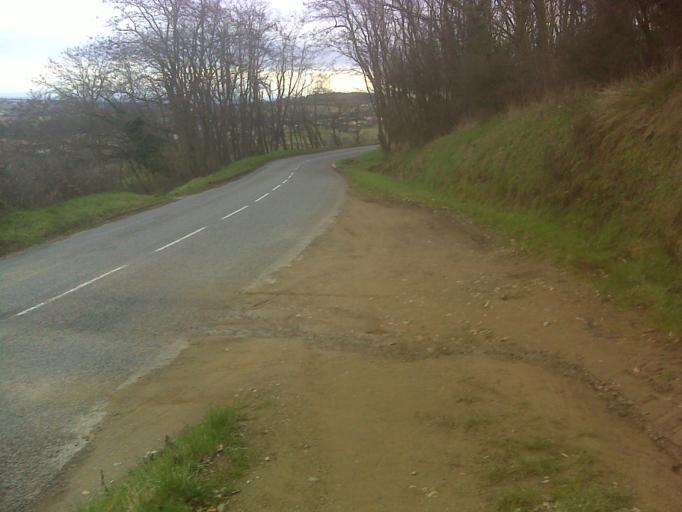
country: FR
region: Rhone-Alpes
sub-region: Departement du Rhone
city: Lentilly
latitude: 45.8195
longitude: 4.6414
